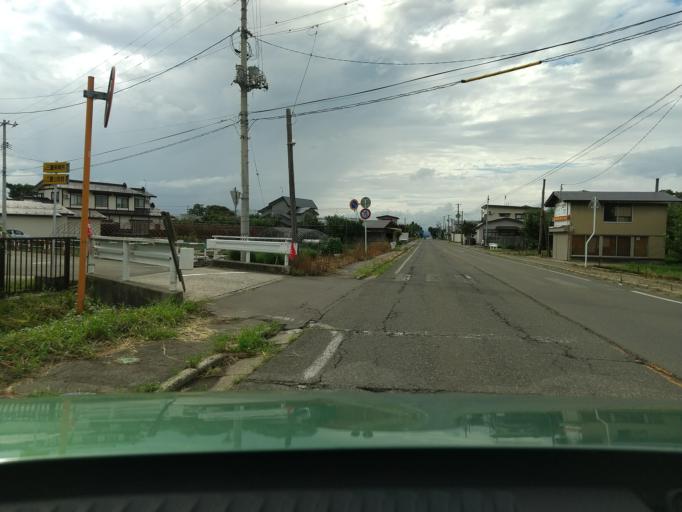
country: JP
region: Akita
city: Yuzawa
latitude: 39.2315
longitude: 140.5147
